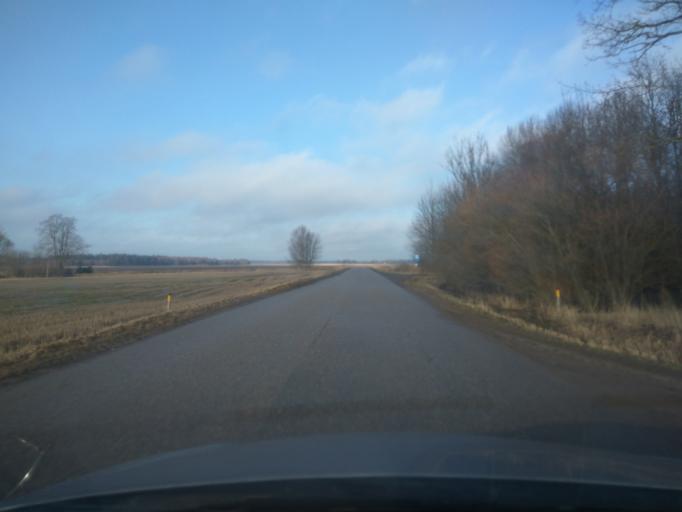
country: LV
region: Saldus Rajons
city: Saldus
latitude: 56.7997
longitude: 22.3814
